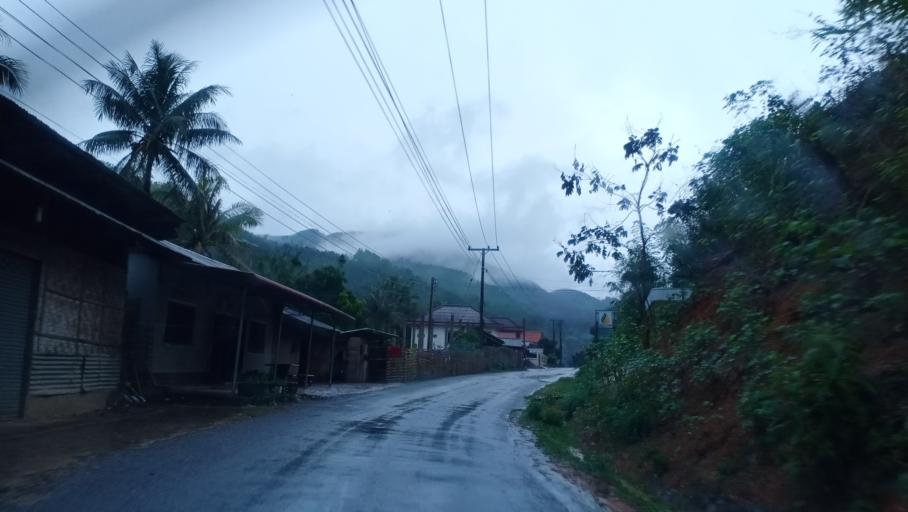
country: LA
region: Phongsali
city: Khoa
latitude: 21.0692
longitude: 102.4908
